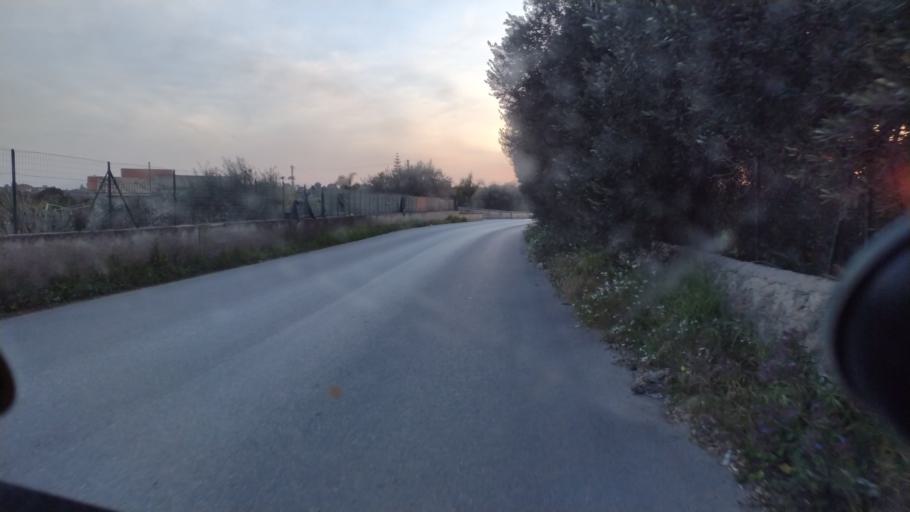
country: IT
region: Sicily
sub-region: Provincia di Siracusa
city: Avola
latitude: 36.8794
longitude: 15.1298
